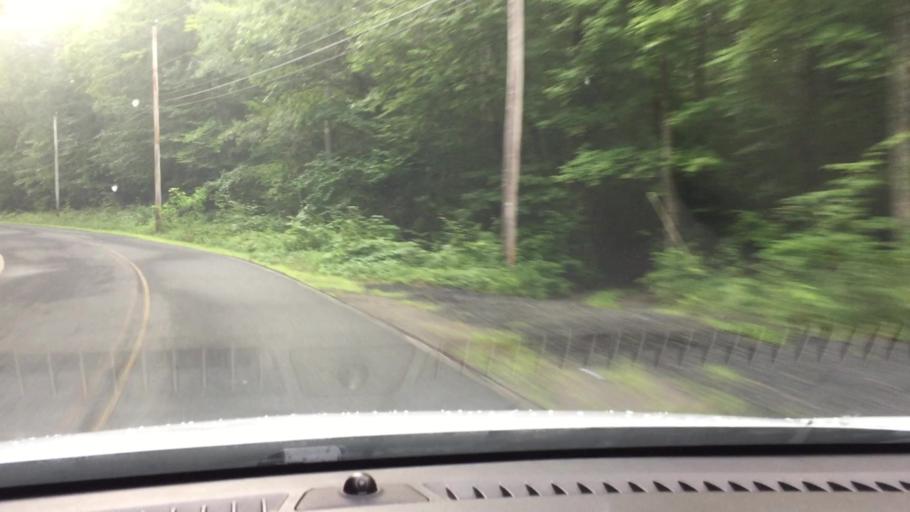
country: US
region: Massachusetts
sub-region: Hampshire County
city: Westhampton
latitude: 42.2524
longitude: -72.9300
